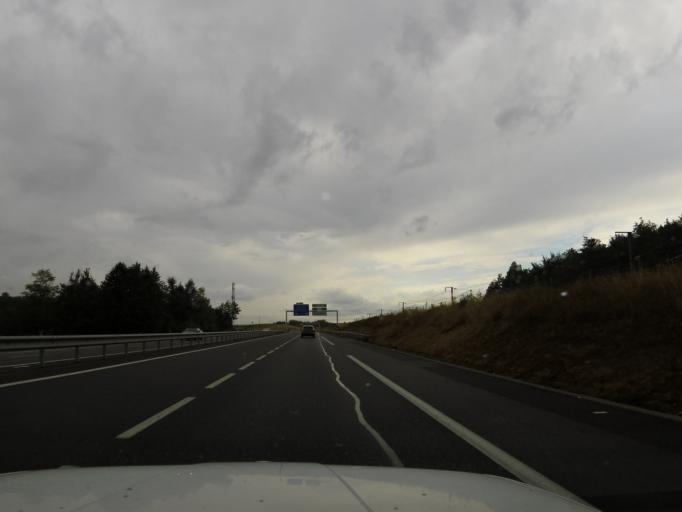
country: FR
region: Rhone-Alpes
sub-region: Departement du Rhone
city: Pusignan
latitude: 45.7718
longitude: 5.0833
